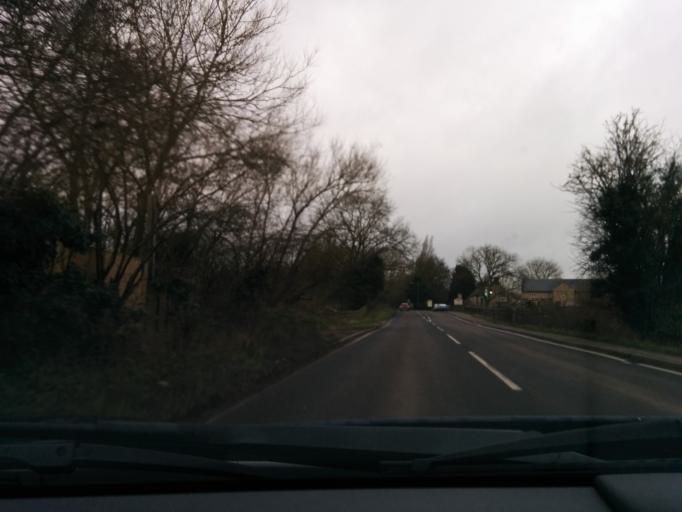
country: GB
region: England
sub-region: Oxfordshire
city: Eynsham
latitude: 51.7763
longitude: -1.3623
